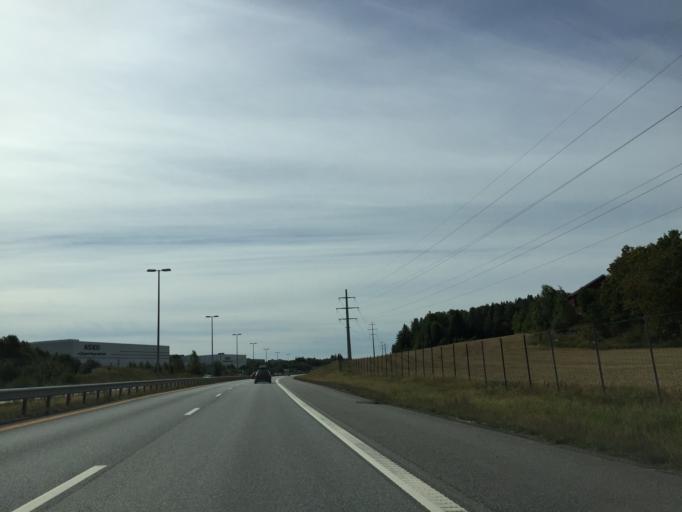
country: NO
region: Akershus
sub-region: Vestby
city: Vestby
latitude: 59.5954
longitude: 10.7387
